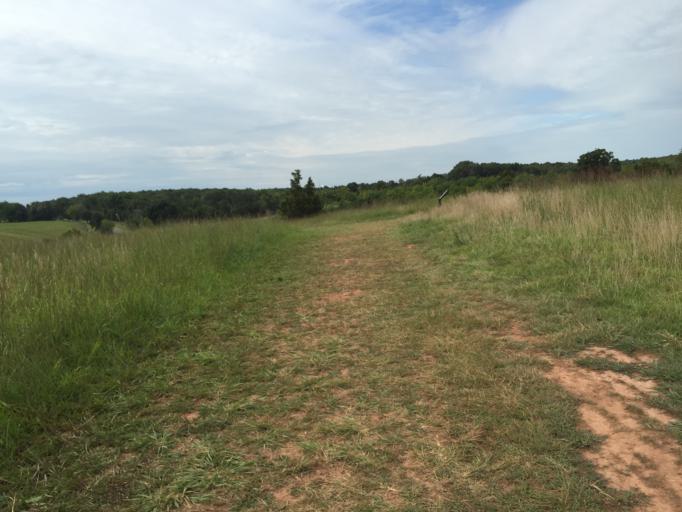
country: US
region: Virginia
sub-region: Prince William County
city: Bull Run
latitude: 38.8204
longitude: -77.5265
